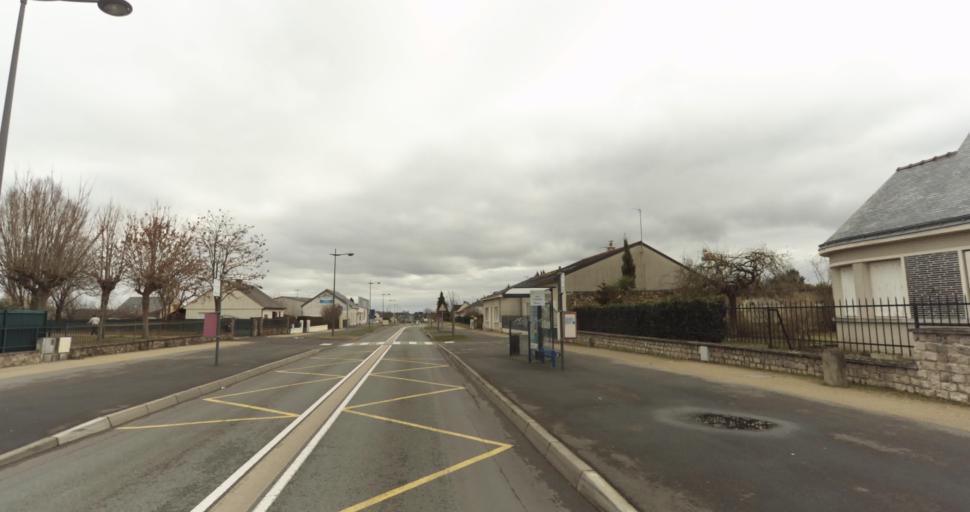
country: FR
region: Pays de la Loire
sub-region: Departement de Maine-et-Loire
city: Jumelles
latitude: 47.3765
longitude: -0.1044
